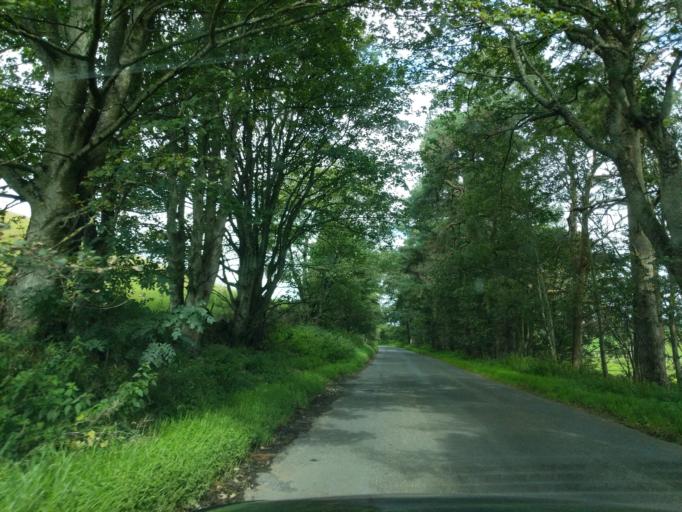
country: GB
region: Scotland
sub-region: The Scottish Borders
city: Peebles
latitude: 55.6359
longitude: -3.2845
